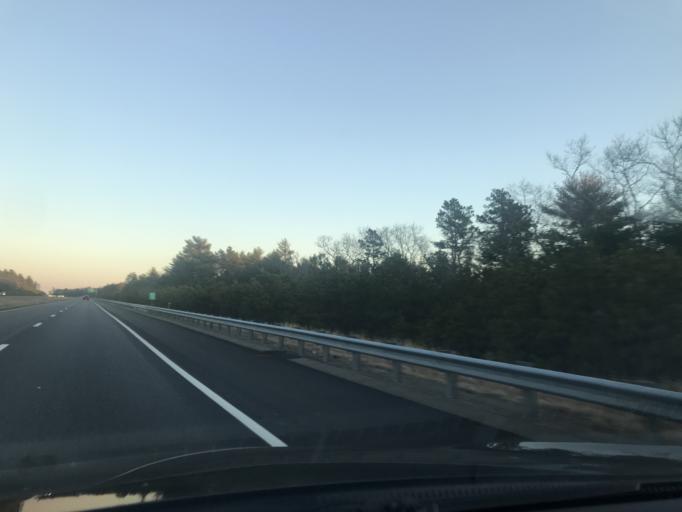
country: US
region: Massachusetts
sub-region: Plymouth County
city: Kingston
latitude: 41.9604
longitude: -70.7324
